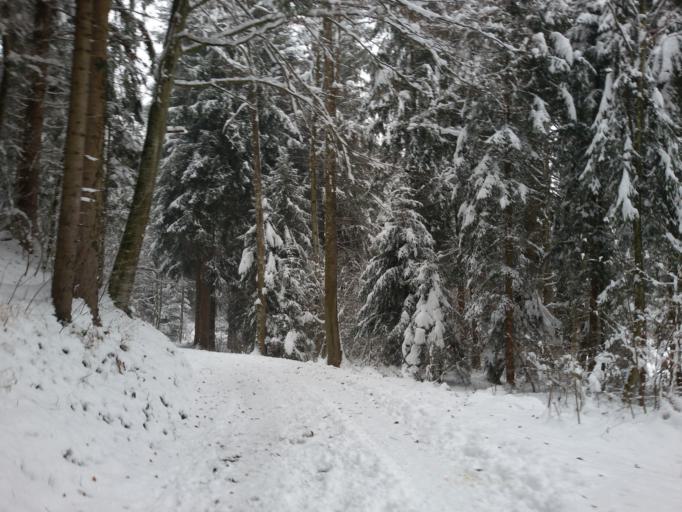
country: CH
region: Zurich
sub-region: Bezirk Hinwil
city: Rueti / Westlicher Dorfteil
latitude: 47.2529
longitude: 8.8301
